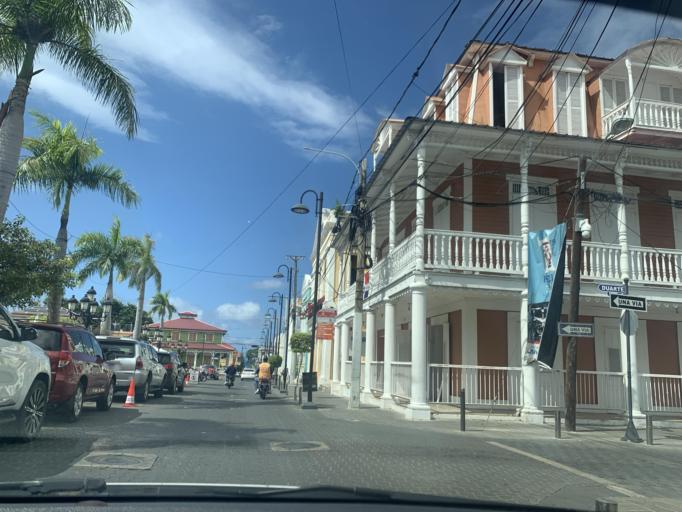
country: DO
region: Puerto Plata
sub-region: Puerto Plata
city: Puerto Plata
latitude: 19.7972
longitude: -70.6932
